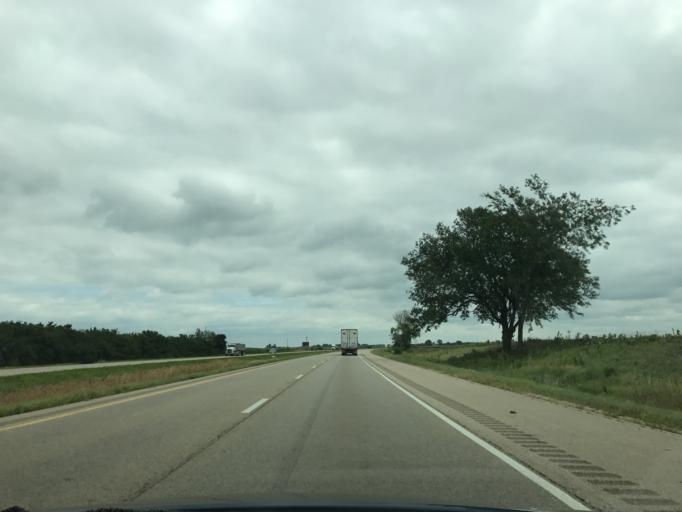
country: US
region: Illinois
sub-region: Bureau County
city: Princeton
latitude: 41.3988
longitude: -89.4180
